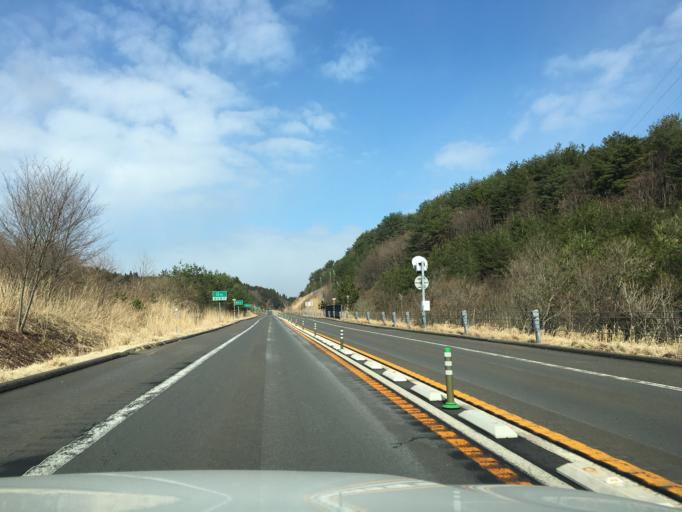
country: JP
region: Akita
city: Akita
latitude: 39.7609
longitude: 140.1303
